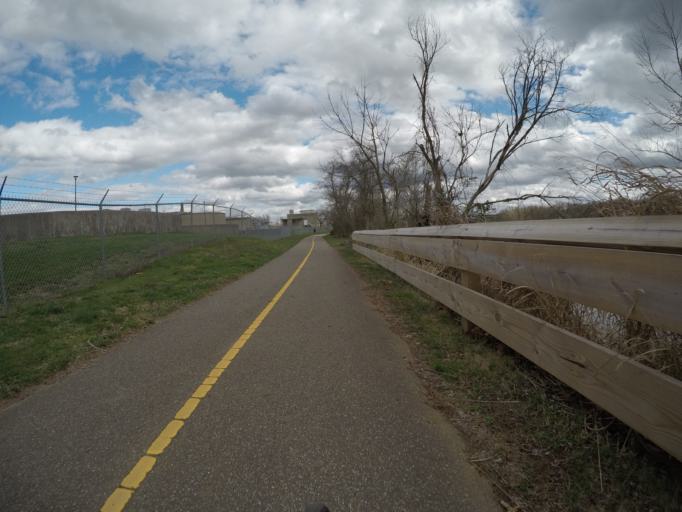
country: US
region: West Virginia
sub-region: Wood County
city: Williamstown
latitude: 39.4088
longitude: -81.4349
